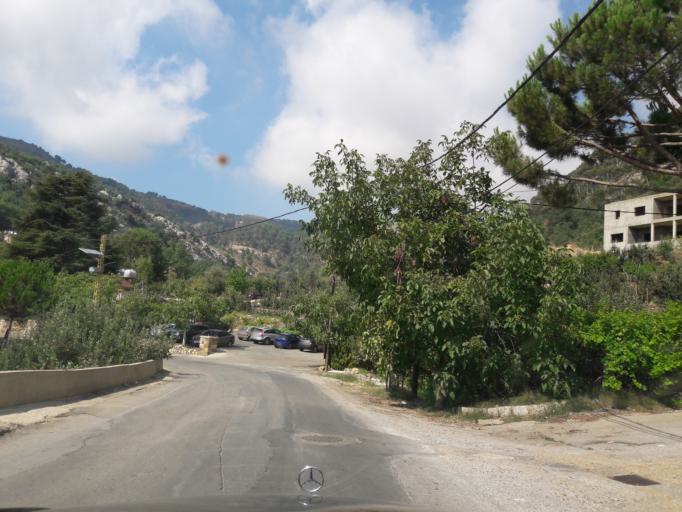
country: LB
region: Mont-Liban
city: Djounie
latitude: 33.9624
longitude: 35.7802
